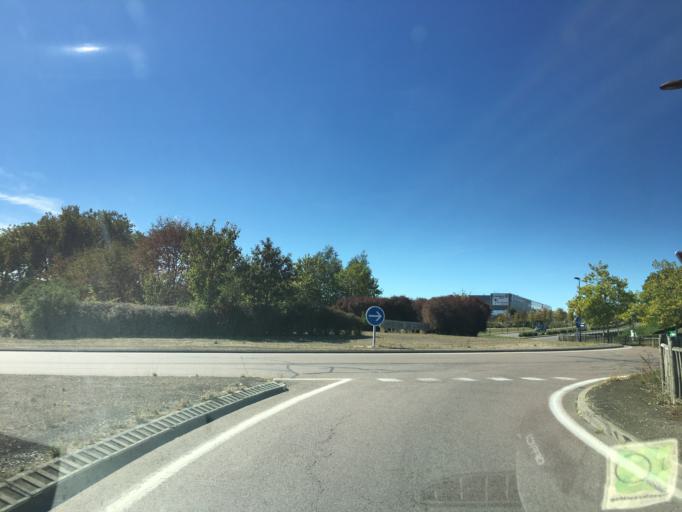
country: FR
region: Bourgogne
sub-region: Departement de l'Yonne
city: Auxerre
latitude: 47.8170
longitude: 3.5606
